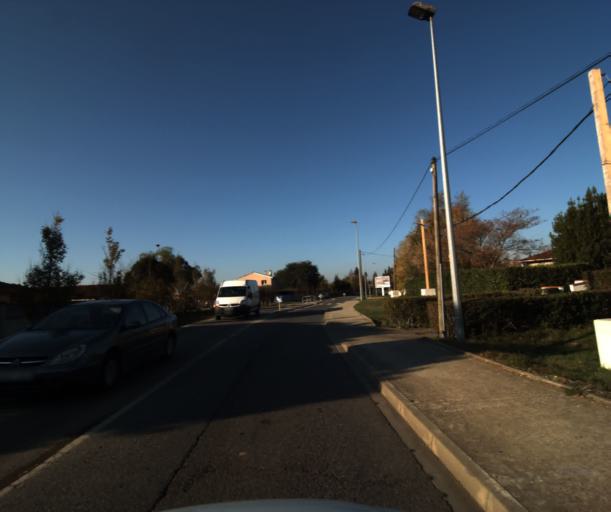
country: FR
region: Midi-Pyrenees
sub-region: Departement de la Haute-Garonne
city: Colomiers
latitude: 43.6225
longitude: 1.3337
